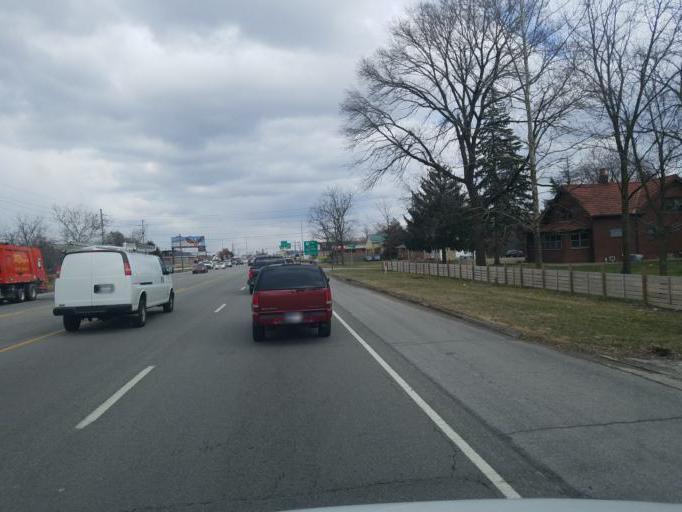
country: US
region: Indiana
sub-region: Marion County
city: Speedway
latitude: 39.7645
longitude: -86.2740
